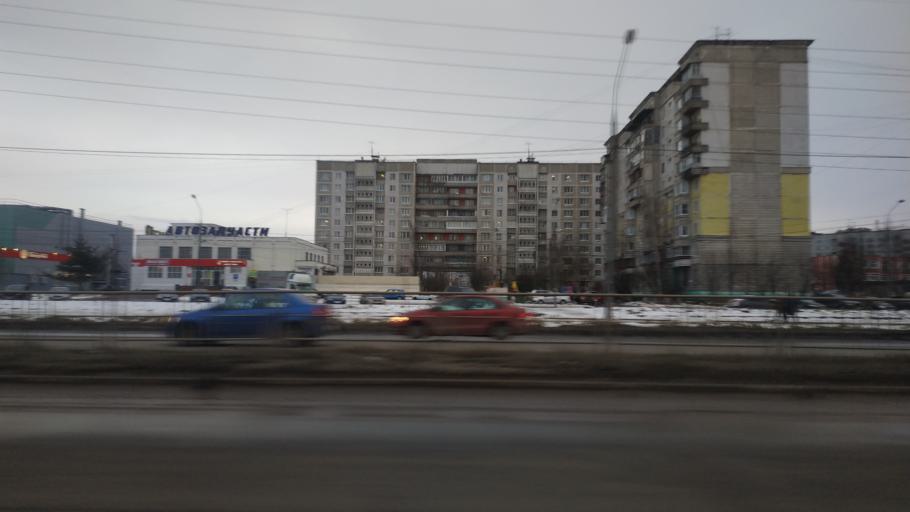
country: RU
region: Tverskaya
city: Tver
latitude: 56.8226
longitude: 35.8899
